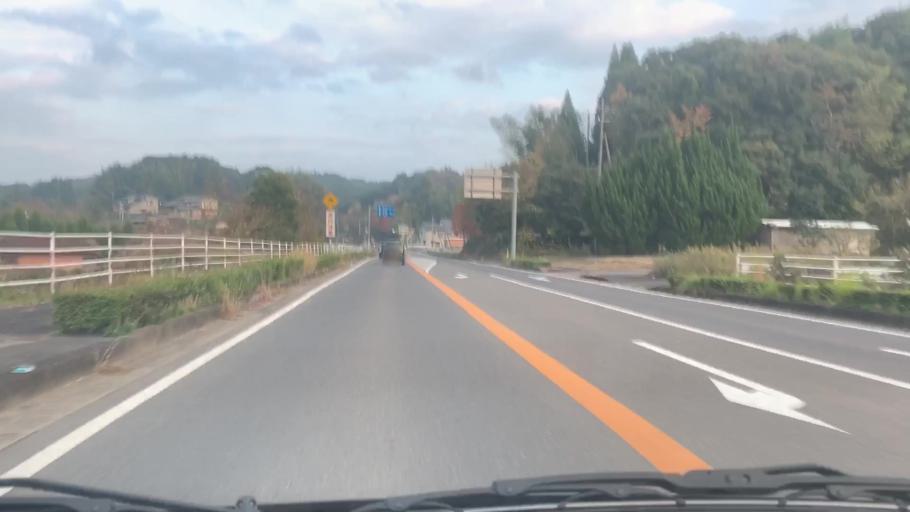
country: JP
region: Saga Prefecture
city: Takeocho-takeo
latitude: 33.1882
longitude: 129.9264
